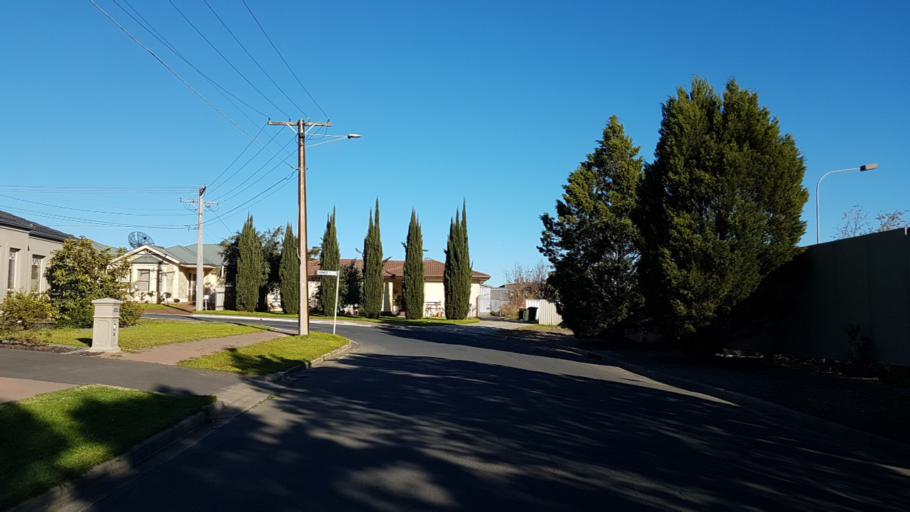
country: AU
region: South Australia
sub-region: Campbelltown
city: Athelstone
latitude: -34.8773
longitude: 138.6858
